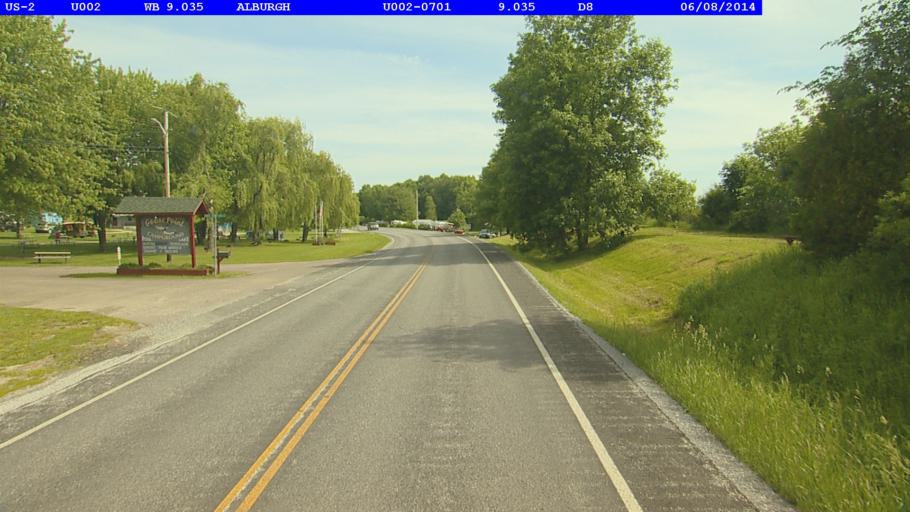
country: US
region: Vermont
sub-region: Grand Isle County
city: North Hero
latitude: 44.9205
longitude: -73.2744
